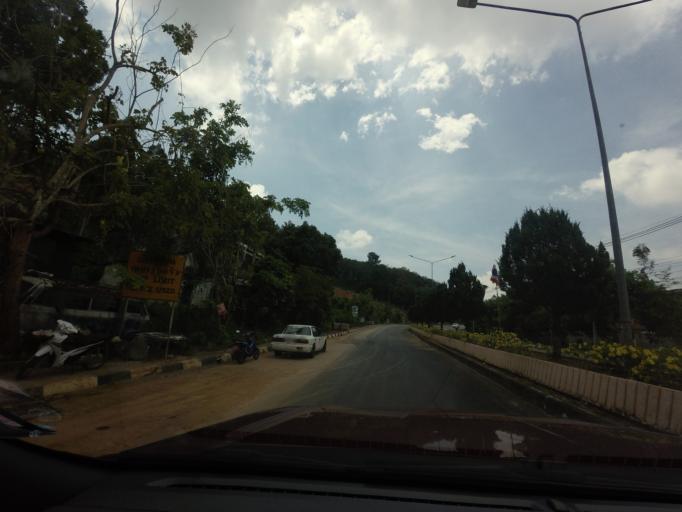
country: TH
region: Yala
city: Betong
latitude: 5.7680
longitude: 101.0573
